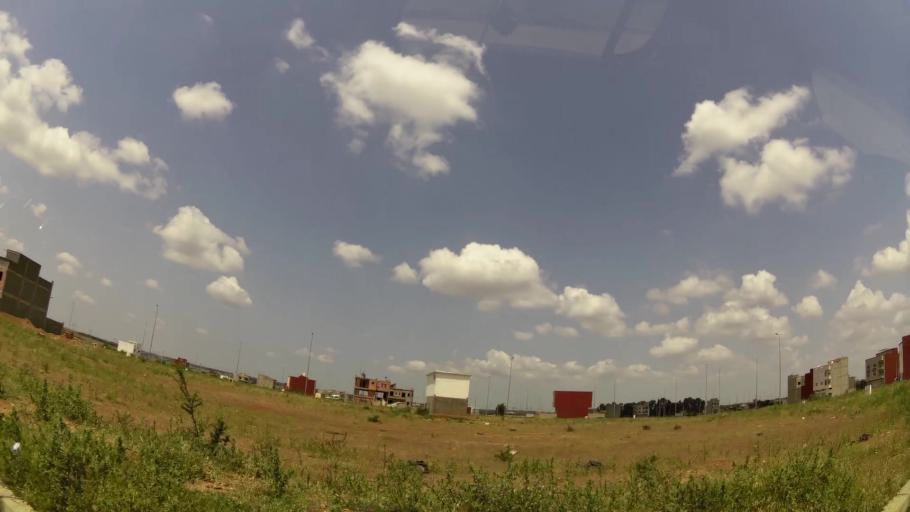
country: MA
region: Rabat-Sale-Zemmour-Zaer
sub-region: Khemisset
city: Tiflet
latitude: 34.0028
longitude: -6.5379
